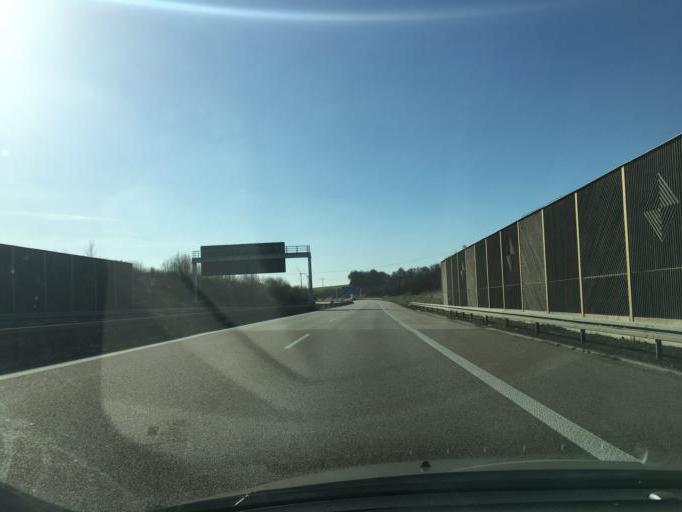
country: DE
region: Saxony
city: Hartmannsdorf
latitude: 50.8627
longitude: 12.8165
